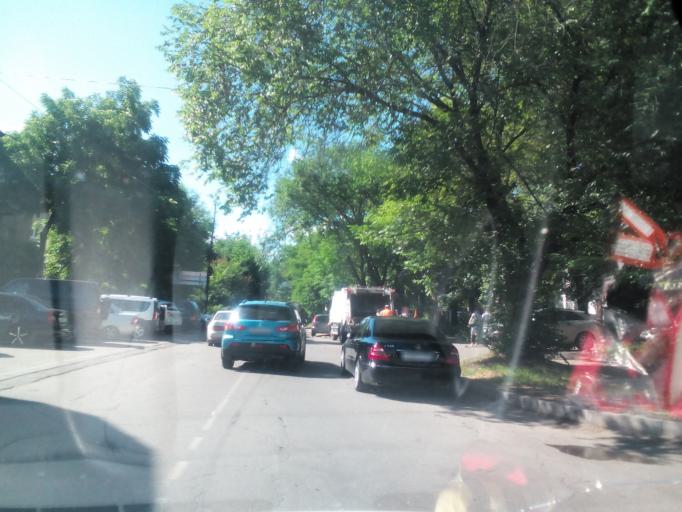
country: RU
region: Stavropol'skiy
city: Pyatigorsk
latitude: 44.0486
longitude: 43.0682
